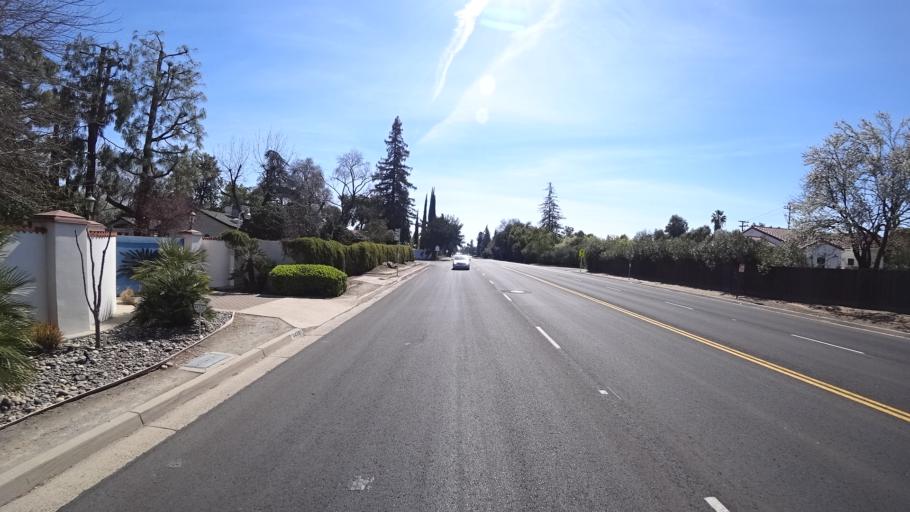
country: US
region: California
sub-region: Fresno County
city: Fresno
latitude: 36.7980
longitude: -119.8085
